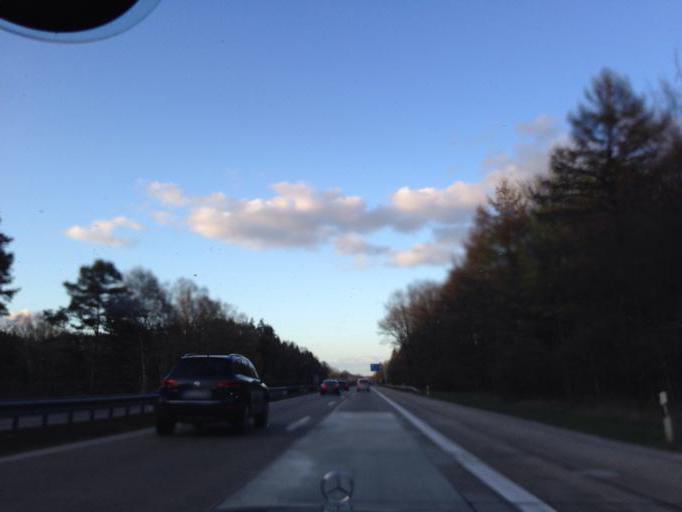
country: DE
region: Lower Saxony
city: Bad Fallingbostel
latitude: 52.8785
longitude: 9.7506
